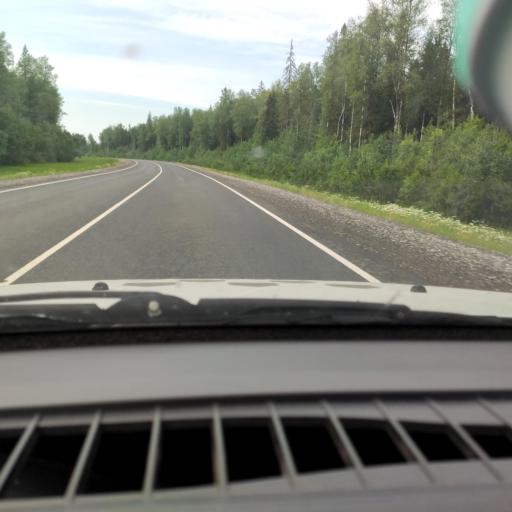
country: RU
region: Kirov
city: Kostino
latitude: 58.6889
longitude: 53.7395
